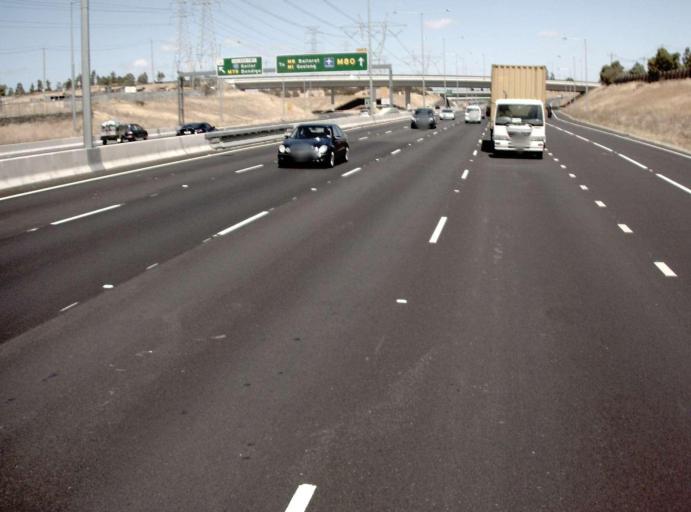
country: AU
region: Victoria
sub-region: Moonee Valley
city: Keilor East
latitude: -37.7240
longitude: 144.8645
